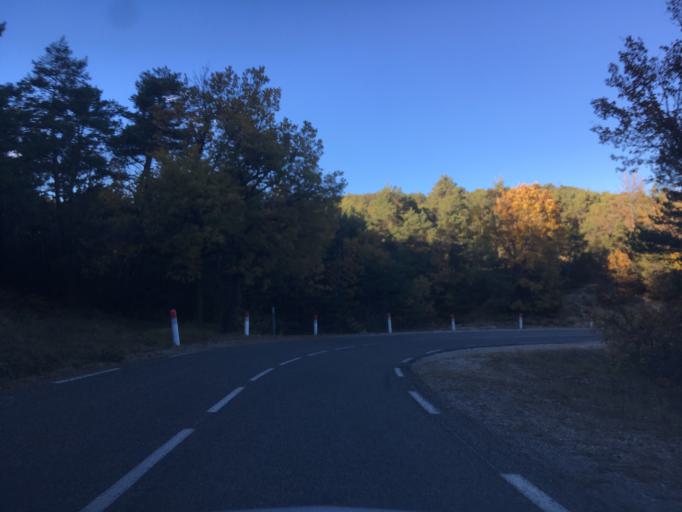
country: FR
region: Provence-Alpes-Cote d'Azur
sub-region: Departement du Var
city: Montferrat
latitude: 43.7211
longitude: 6.5012
